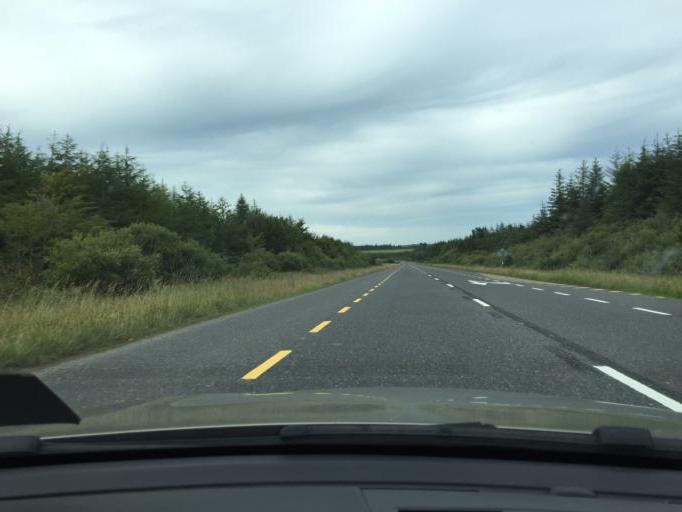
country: IE
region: Munster
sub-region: Waterford
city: Dungarvan
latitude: 52.0165
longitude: -7.6947
